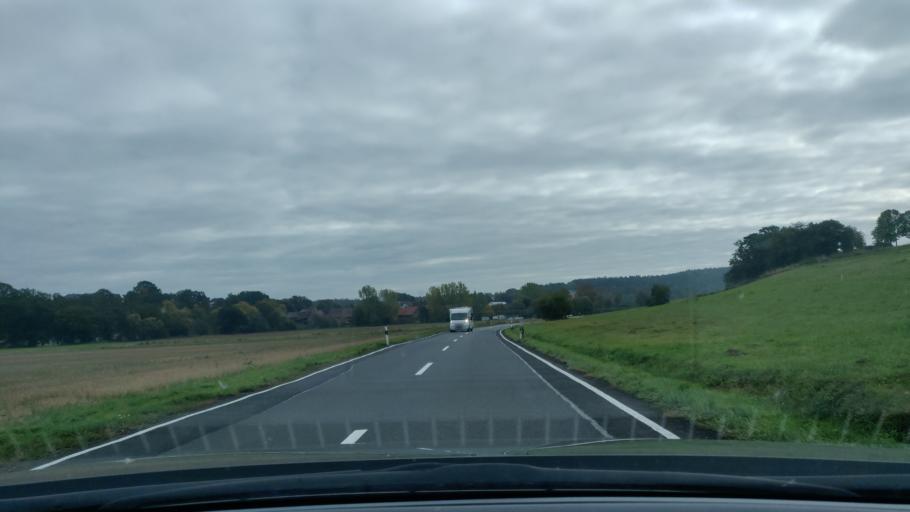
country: DE
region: Hesse
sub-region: Regierungsbezirk Kassel
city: Neuental
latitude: 50.9998
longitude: 9.2031
